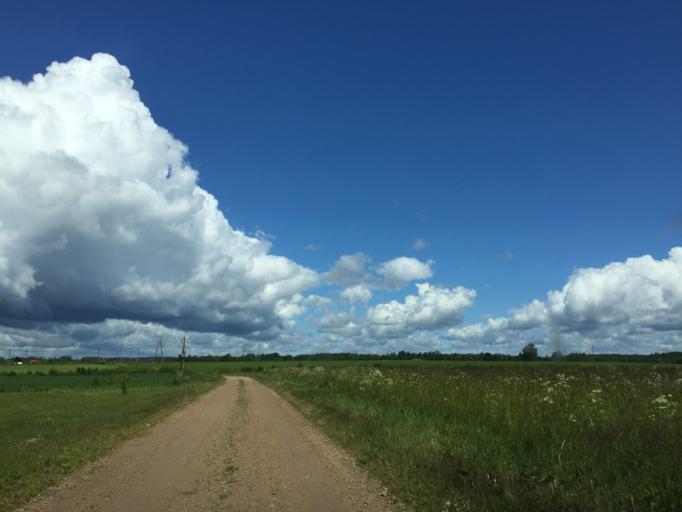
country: LV
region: Lecava
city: Iecava
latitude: 56.6154
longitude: 24.2088
